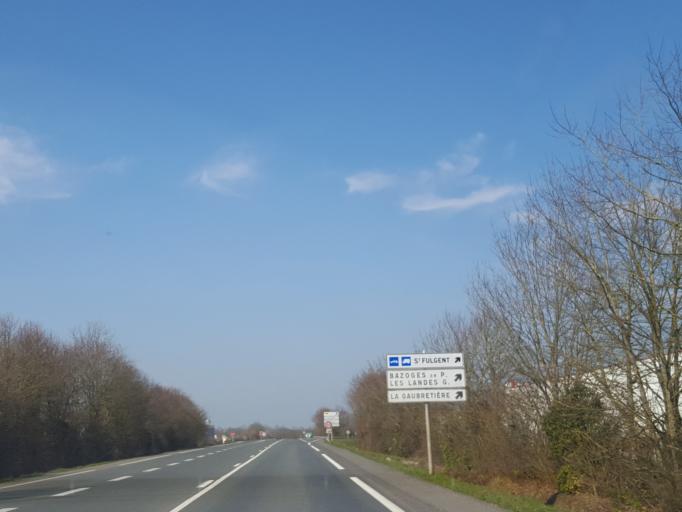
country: FR
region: Pays de la Loire
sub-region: Departement de la Vendee
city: Saint-Fulgent
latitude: 46.8568
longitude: -1.1691
